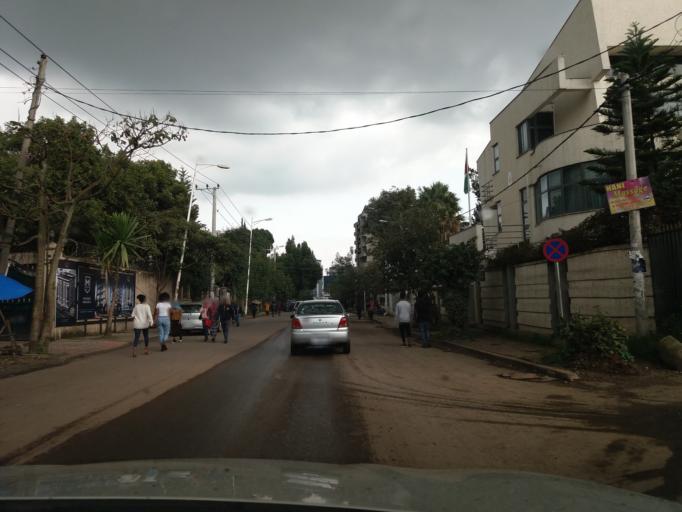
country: ET
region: Adis Abeba
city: Addis Ababa
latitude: 8.9932
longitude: 38.7849
